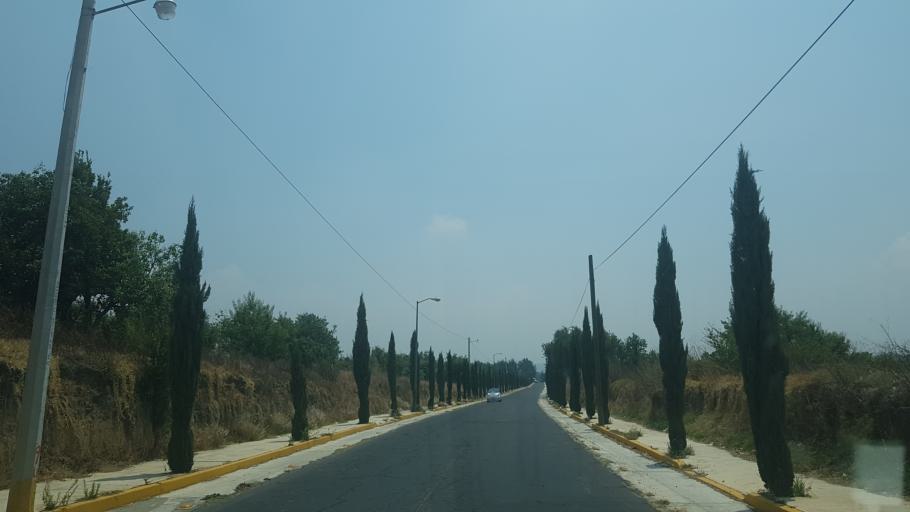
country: MX
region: Puebla
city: San Andres Calpan
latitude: 19.1030
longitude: -98.4469
